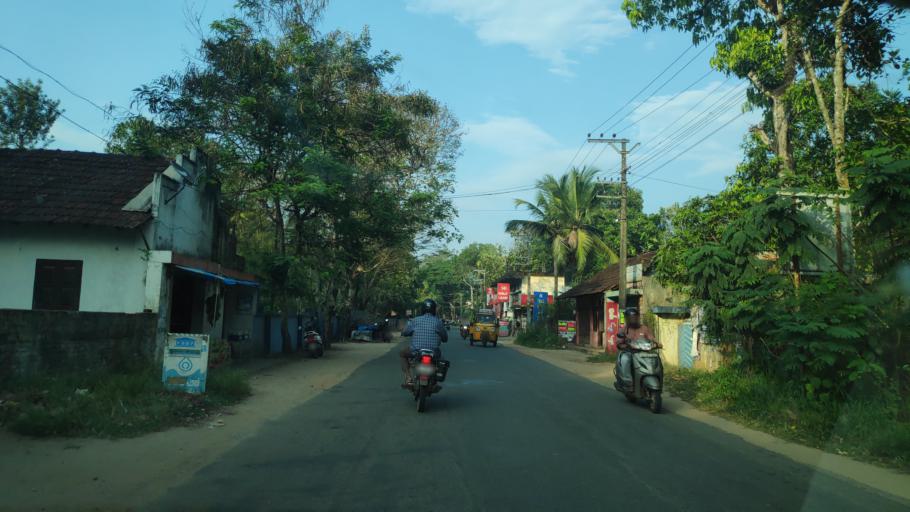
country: IN
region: Kerala
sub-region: Alappuzha
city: Shertallai
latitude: 9.6072
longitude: 76.3604
